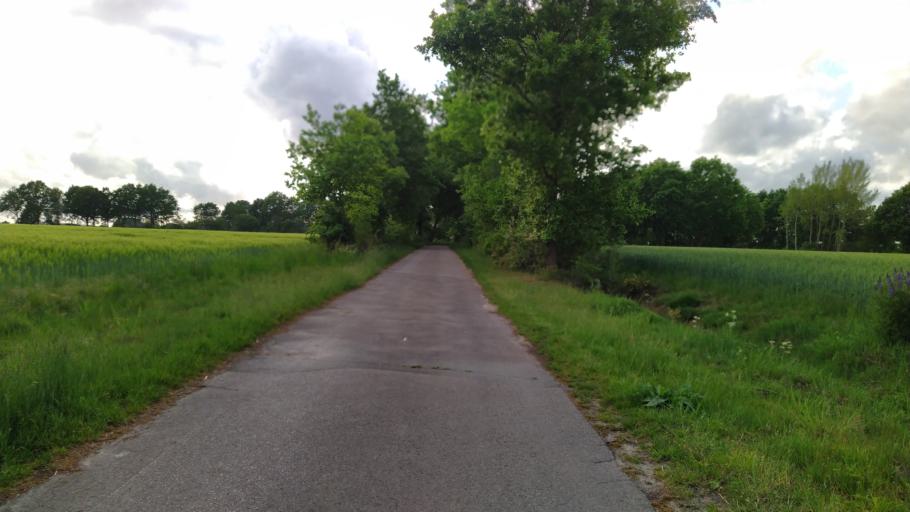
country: DE
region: Lower Saxony
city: Kutenholz
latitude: 53.4682
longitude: 9.3207
